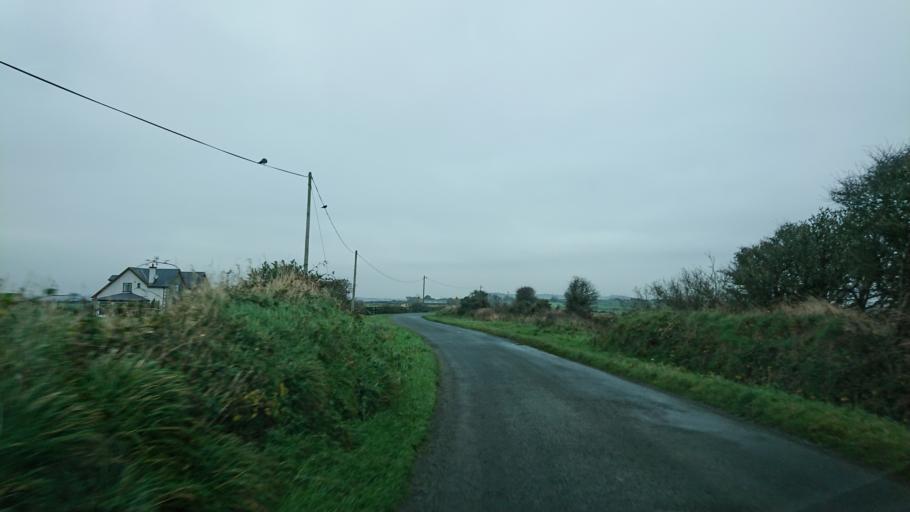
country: IE
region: Munster
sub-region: Waterford
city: Dunmore East
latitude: 52.1507
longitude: -7.0454
